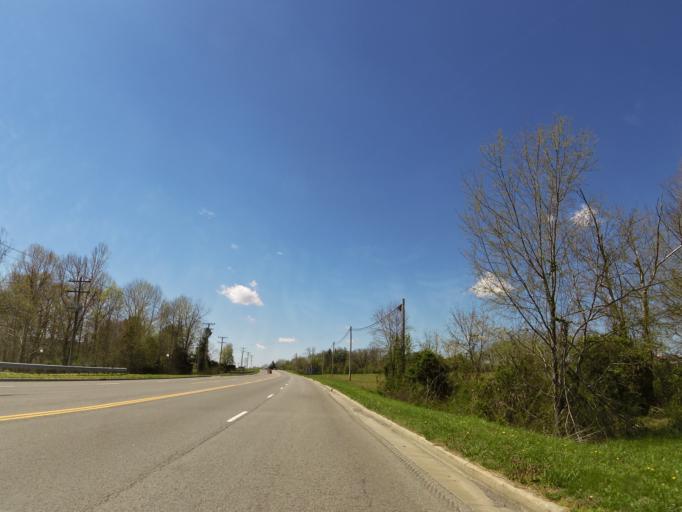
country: US
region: Tennessee
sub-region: DeKalb County
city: Smithville
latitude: 35.9576
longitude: -85.7876
